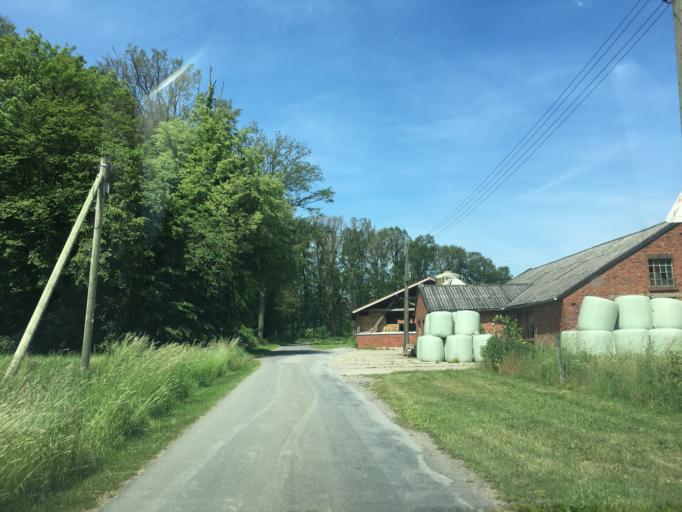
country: DE
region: North Rhine-Westphalia
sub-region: Regierungsbezirk Munster
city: Nordwalde
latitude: 52.0495
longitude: 7.5213
